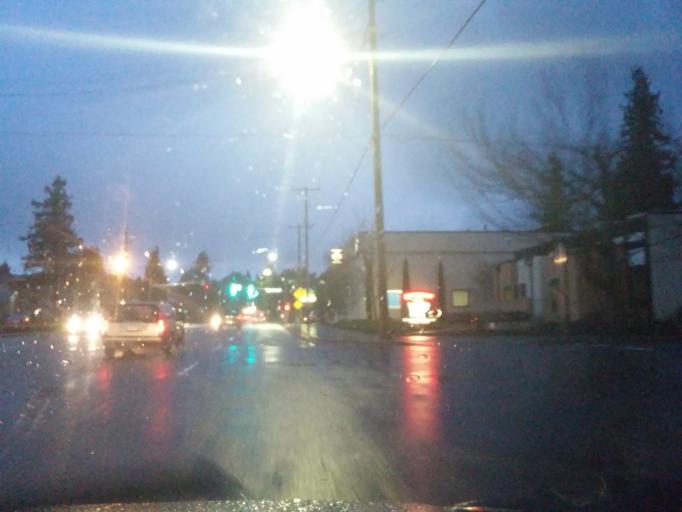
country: US
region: Washington
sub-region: King County
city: Shoreline
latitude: 47.7365
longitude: -122.3127
